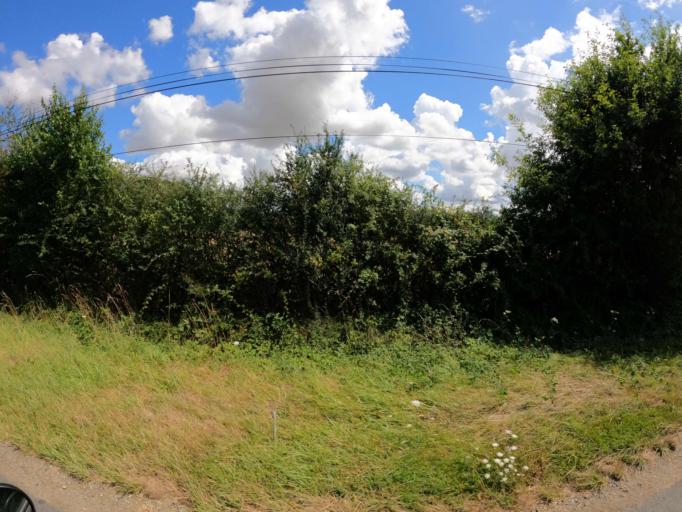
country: FR
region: Pays de la Loire
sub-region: Departement de la Sarthe
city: Juigne-sur-Sarthe
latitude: 47.8975
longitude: -0.2850
